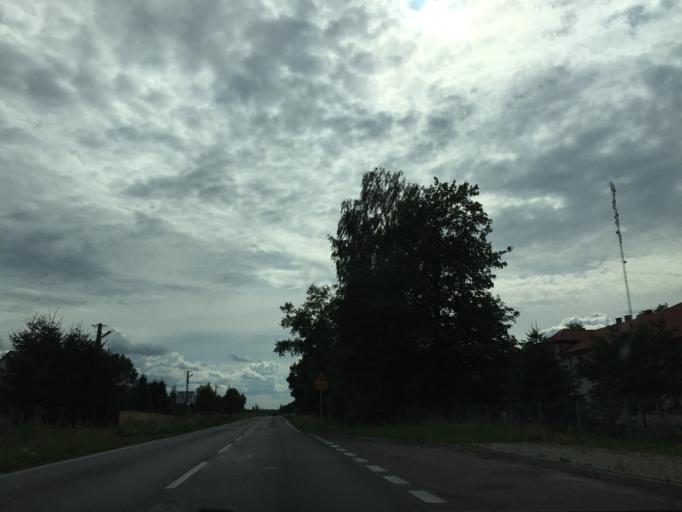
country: PL
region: Lublin Voivodeship
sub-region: Powiat lukowski
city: Trzebieszow
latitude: 51.9590
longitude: 22.4685
